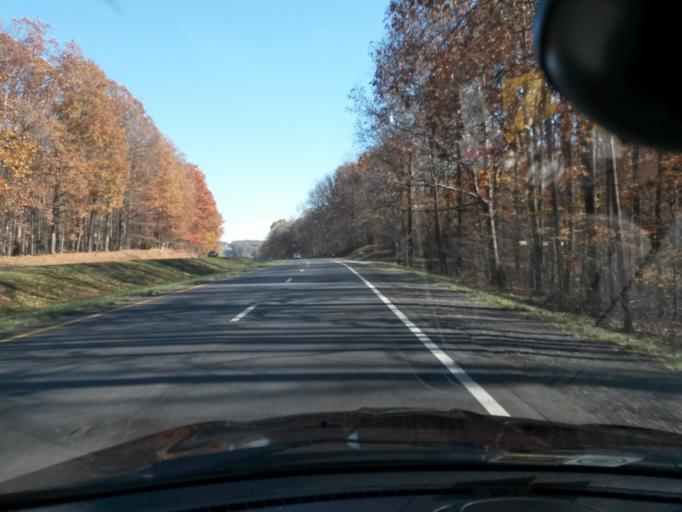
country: US
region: Virginia
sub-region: Bedford County
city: Forest
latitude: 37.3011
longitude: -79.3362
